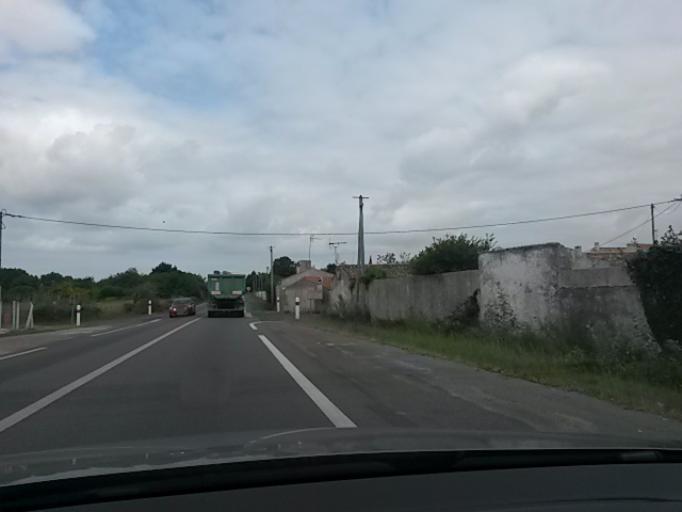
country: FR
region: Poitou-Charentes
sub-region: Departement de la Charente-Maritime
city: Saint-Trojan-les-Bains
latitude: 45.8742
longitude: -1.2224
